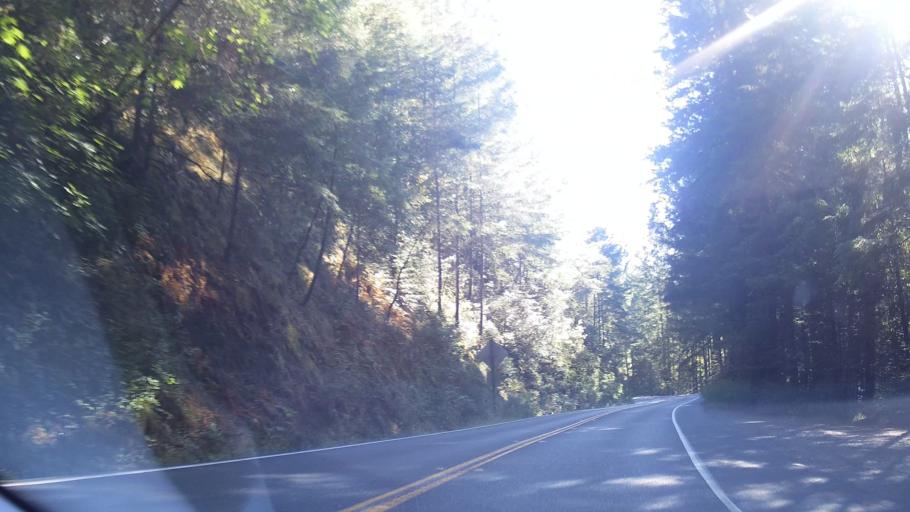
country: US
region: California
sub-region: Mendocino County
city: Brooktrails
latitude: 39.3684
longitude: -123.4967
